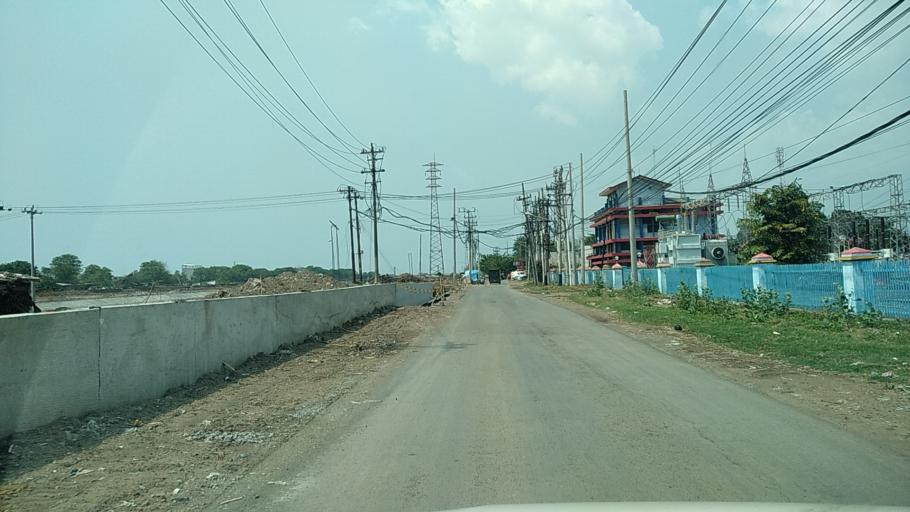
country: ID
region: Central Java
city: Semarang
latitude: -6.9950
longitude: 110.4402
